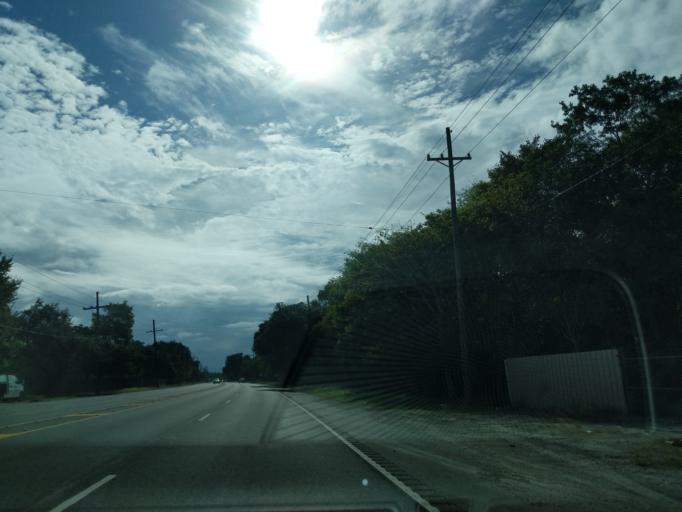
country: US
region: Louisiana
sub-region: Saint Bernard Parish
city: Chalmette
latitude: 30.0469
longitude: -89.8896
